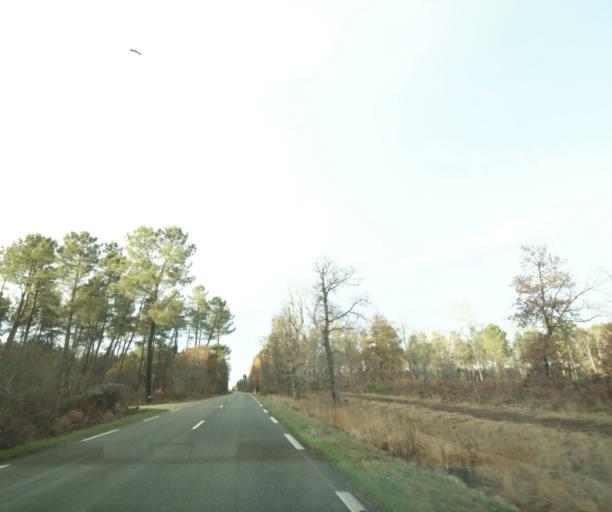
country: FR
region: Aquitaine
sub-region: Departement des Landes
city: Gabarret
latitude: 44.0333
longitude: -0.0309
